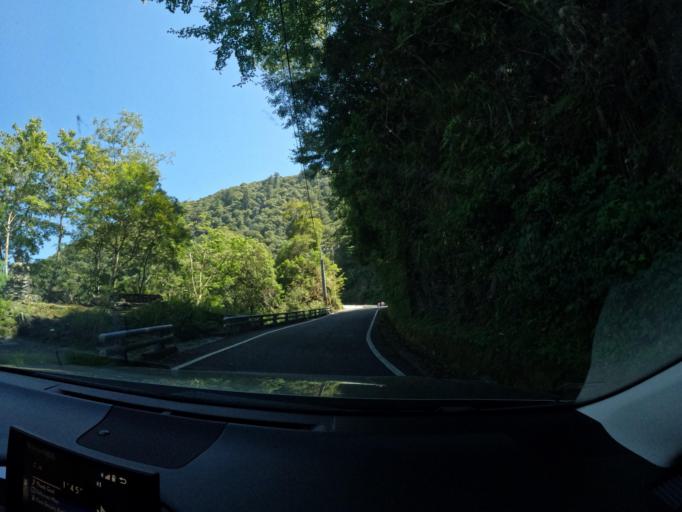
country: TW
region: Taiwan
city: Yujing
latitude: 23.2782
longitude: 120.9077
